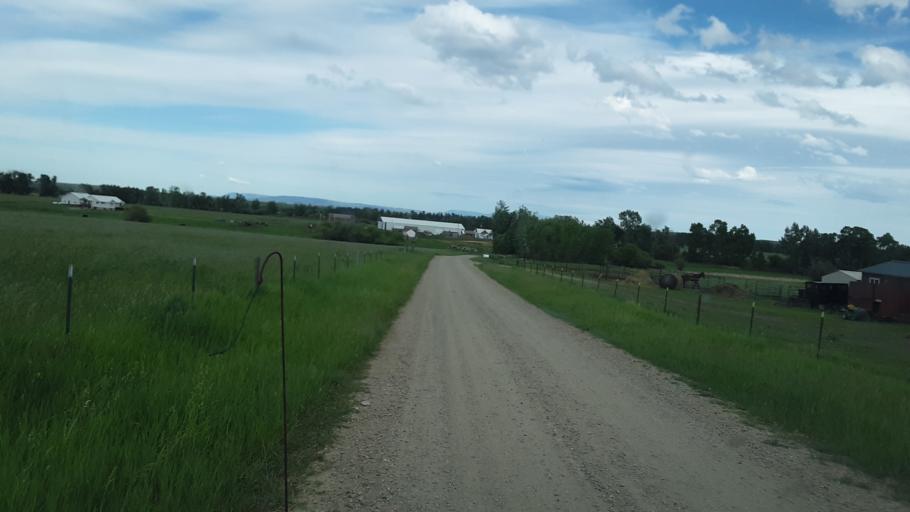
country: US
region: Montana
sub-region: Carbon County
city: Red Lodge
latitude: 45.3634
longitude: -109.1901
